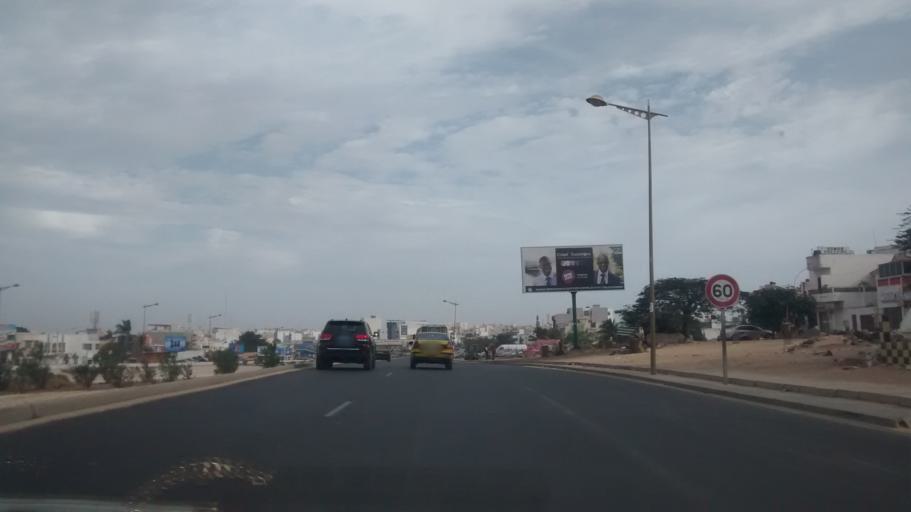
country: SN
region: Dakar
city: Mermoz Boabab
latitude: 14.7185
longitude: -17.4711
